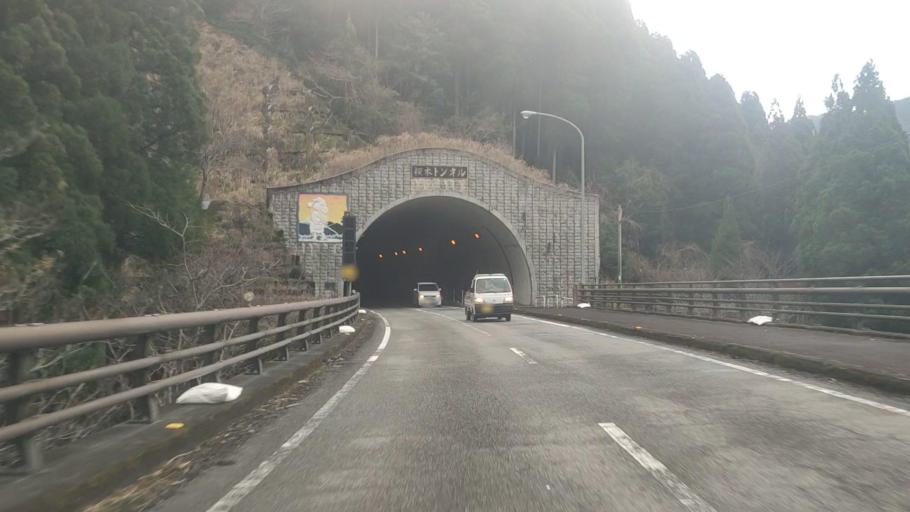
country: JP
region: Kumamoto
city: Hitoyoshi
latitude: 32.3937
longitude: 130.8272
